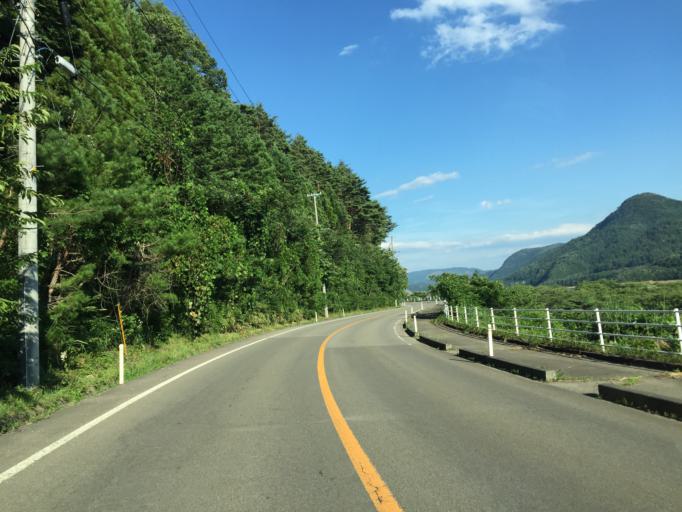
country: JP
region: Miyagi
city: Shiroishi
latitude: 37.9829
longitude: 140.4755
